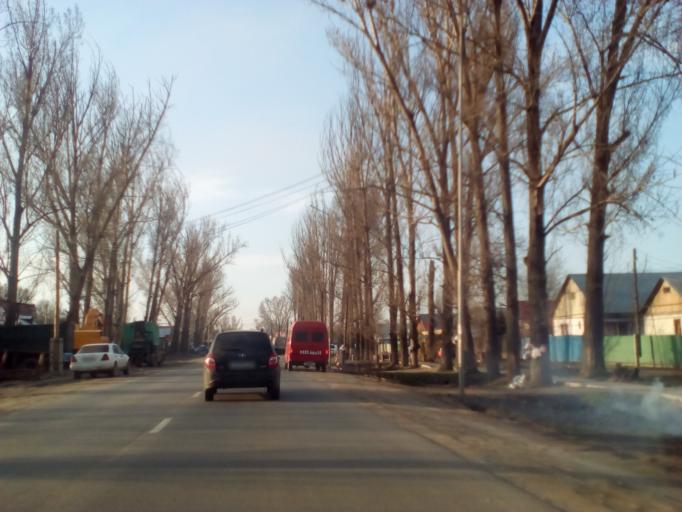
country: KZ
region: Almaty Oblysy
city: Burunday
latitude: 43.2576
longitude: 76.7803
